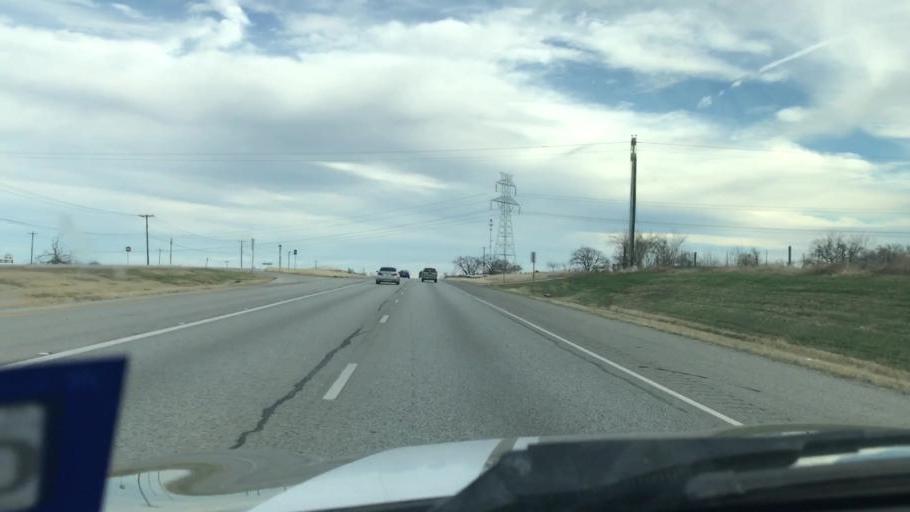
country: US
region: Texas
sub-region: Bastrop County
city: Elgin
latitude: 30.3313
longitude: -97.3494
